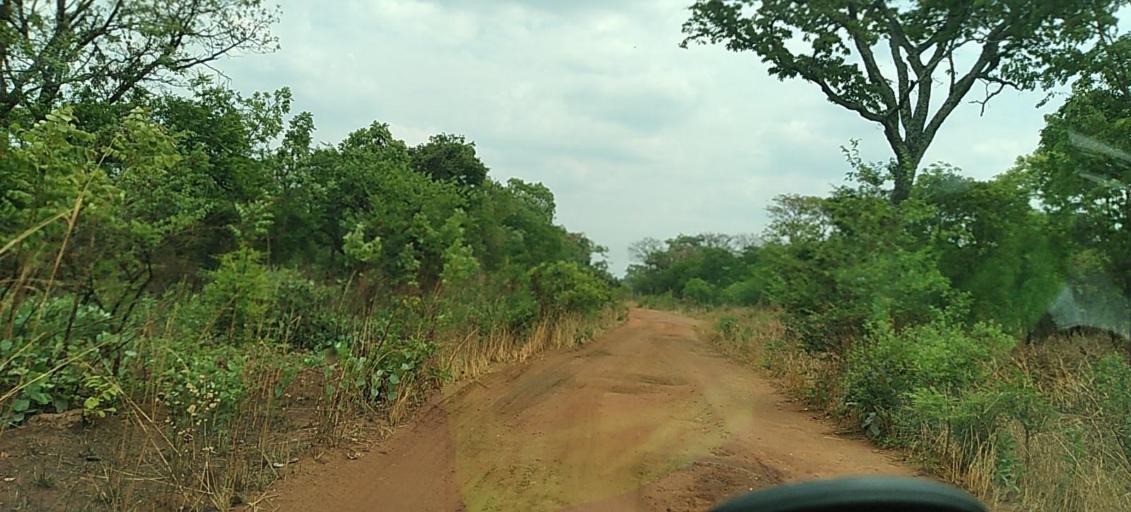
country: ZM
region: North-Western
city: Kansanshi
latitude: -12.0492
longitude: 26.3765
